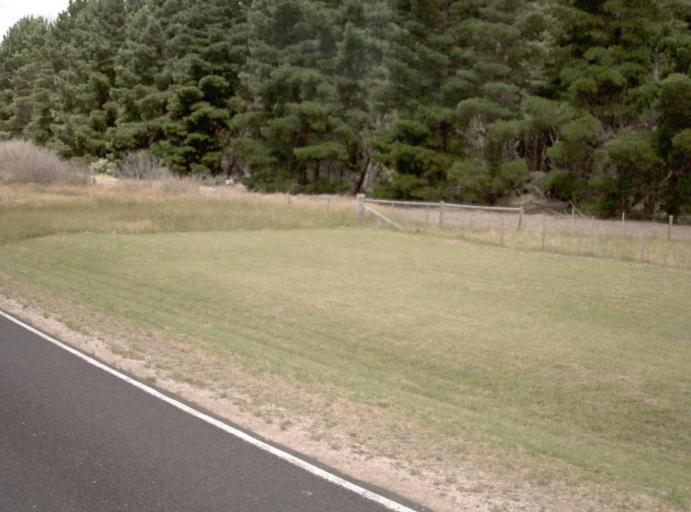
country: AU
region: Victoria
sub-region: Wellington
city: Sale
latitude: -38.1695
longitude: 147.0348
